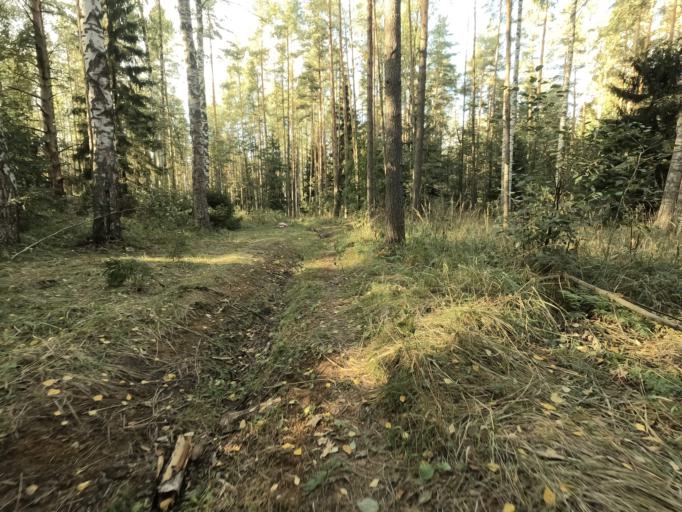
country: RU
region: Leningrad
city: Imeni Sverdlova
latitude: 59.8461
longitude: 30.7299
